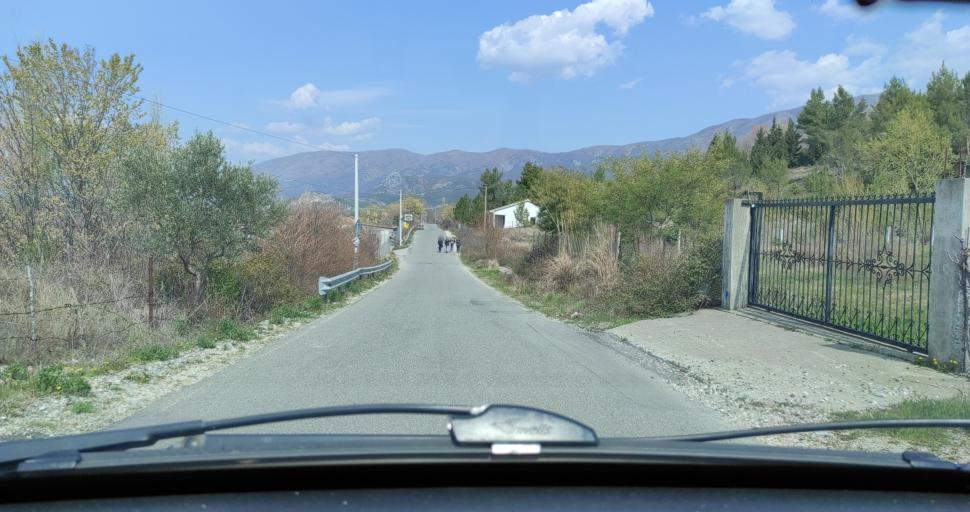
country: AL
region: Lezhe
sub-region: Rrethi i Lezhes
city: Kallmeti i Madh
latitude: 41.8526
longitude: 19.6942
